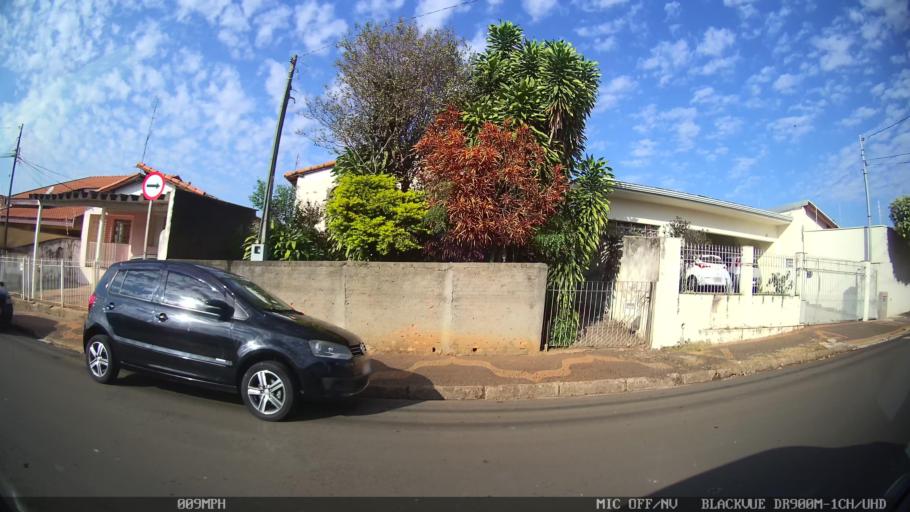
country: BR
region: Sao Paulo
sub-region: Americana
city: Americana
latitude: -22.7438
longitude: -47.3475
